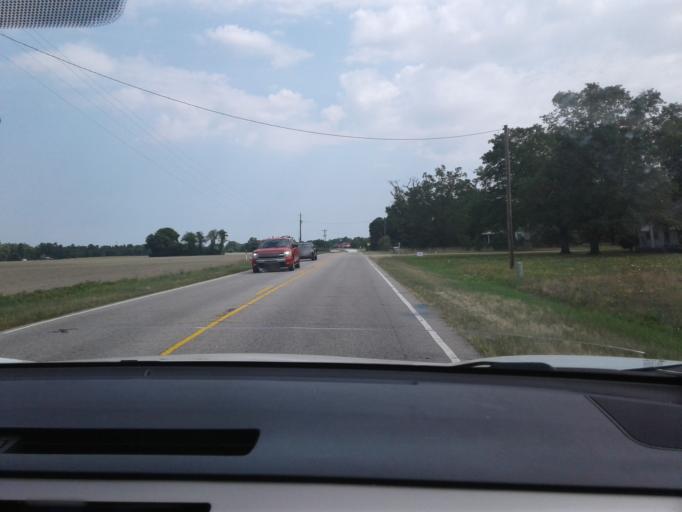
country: US
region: North Carolina
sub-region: Harnett County
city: Erwin
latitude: 35.3655
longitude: -78.6631
